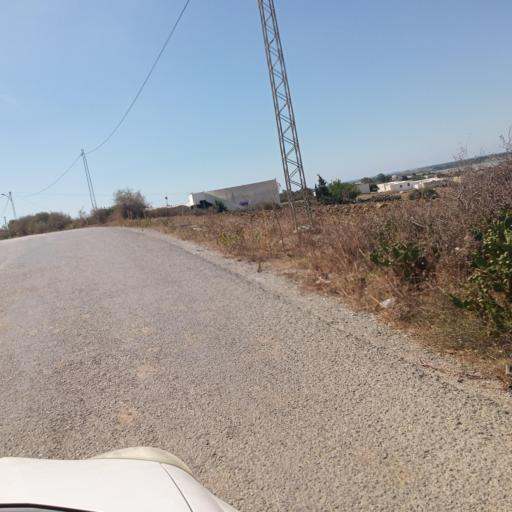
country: TN
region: Nabul
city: Qulaybiyah
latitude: 36.8653
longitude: 11.0333
